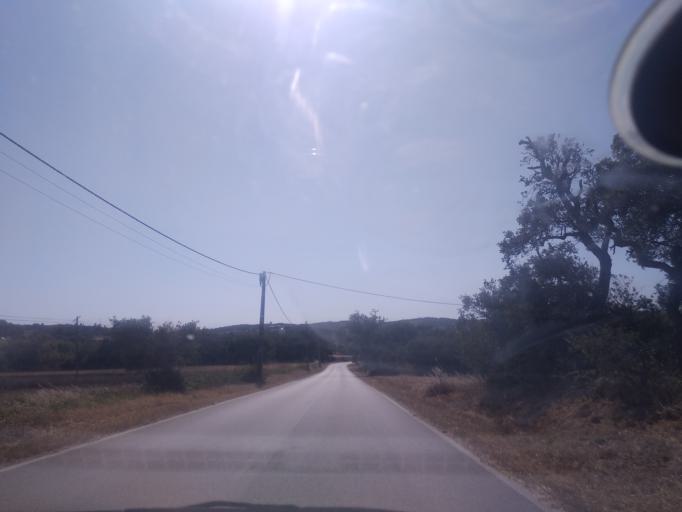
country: PT
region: Faro
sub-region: Aljezur
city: Aljezur
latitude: 37.2275
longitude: -8.8215
